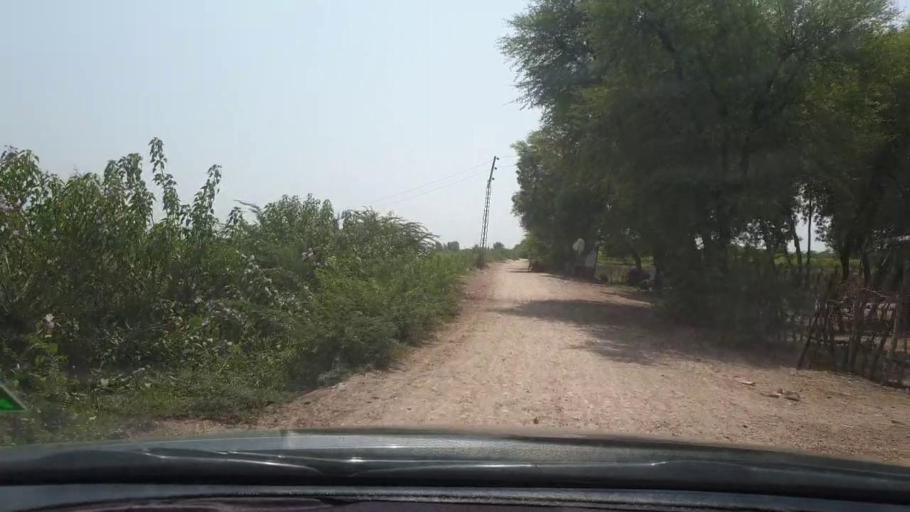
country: PK
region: Sindh
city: Tando Bago
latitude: 24.7816
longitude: 69.1824
